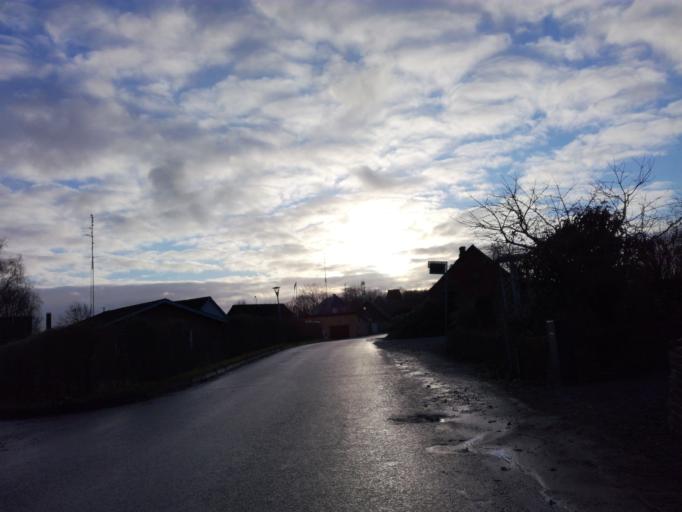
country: DK
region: South Denmark
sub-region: Fredericia Kommune
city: Taulov
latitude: 55.5590
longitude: 9.6040
